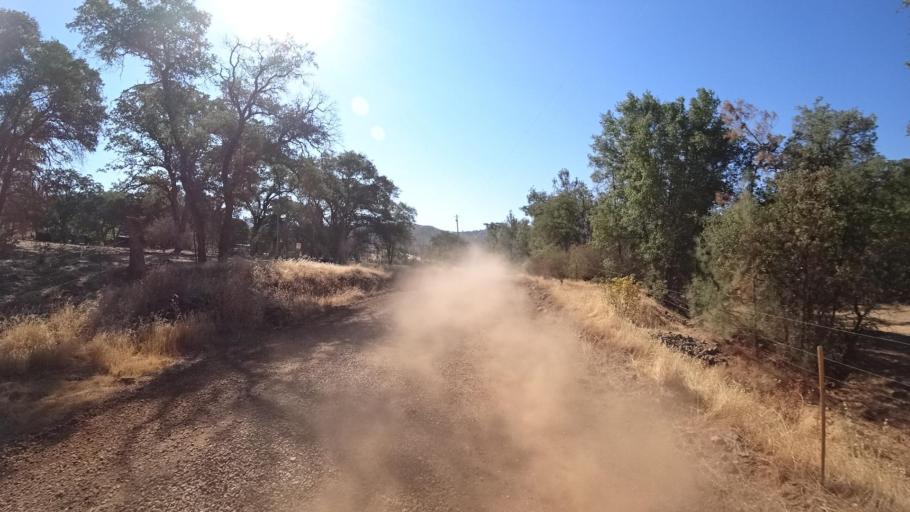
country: US
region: California
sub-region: Mariposa County
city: Mariposa
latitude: 37.6192
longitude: -120.2357
